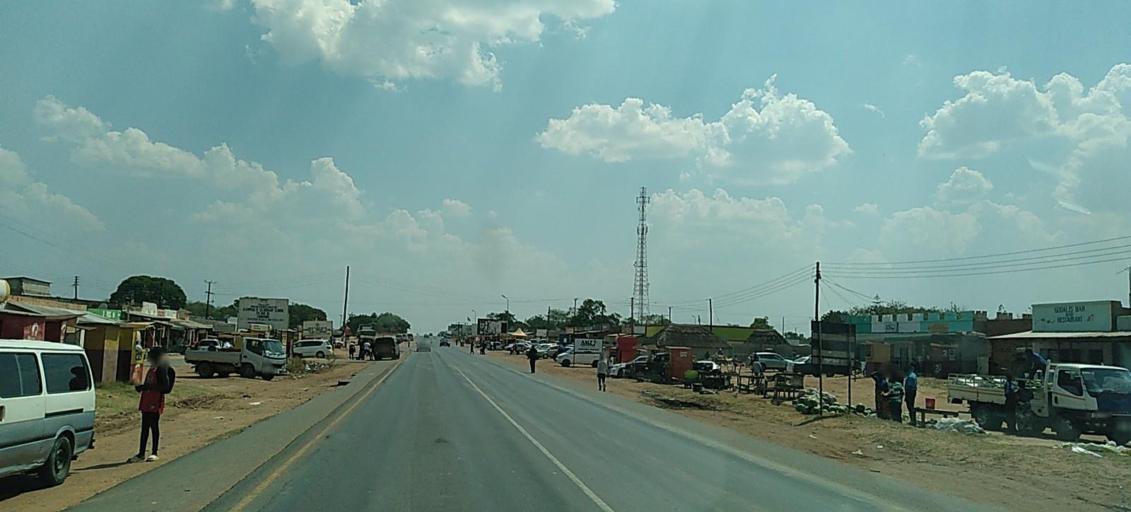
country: ZM
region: Central
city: Chibombo
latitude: -14.6914
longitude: 28.1088
